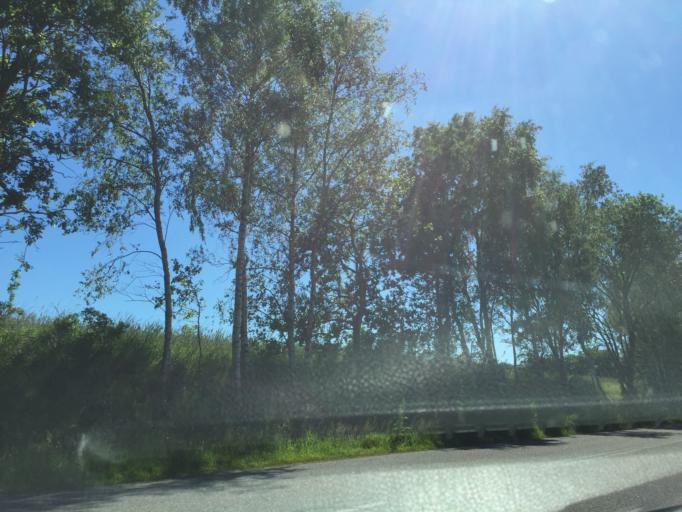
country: DK
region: Central Jutland
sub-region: Viborg Kommune
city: Bjerringbro
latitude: 56.3564
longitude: 9.6685
